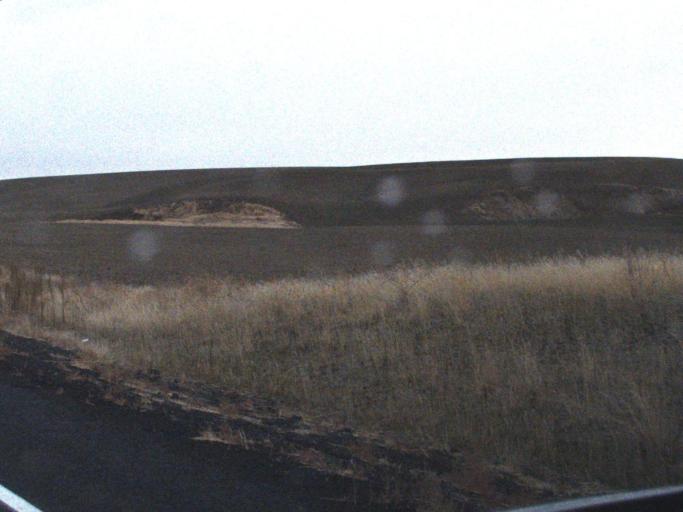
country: US
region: Washington
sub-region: Garfield County
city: Pomeroy
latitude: 46.7902
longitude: -117.8967
